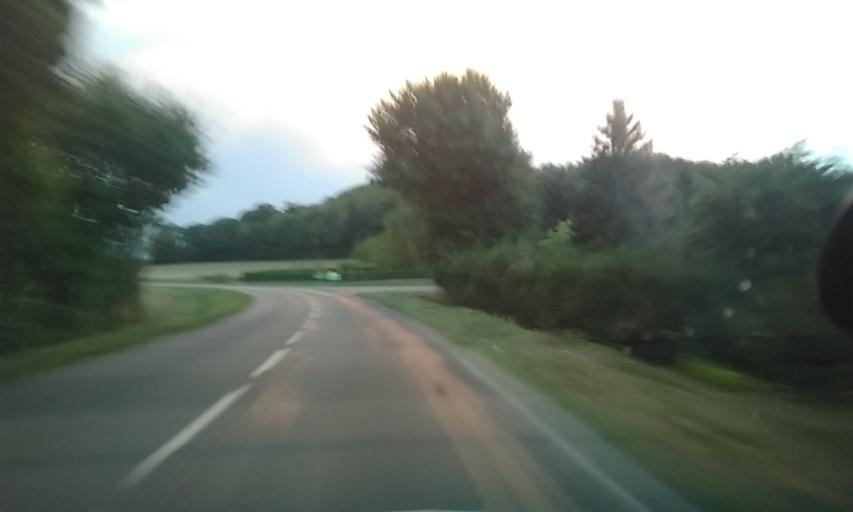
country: FR
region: Brittany
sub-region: Departement d'Ille-et-Vilaine
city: Saint-Thurial
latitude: 48.0581
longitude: -1.9203
